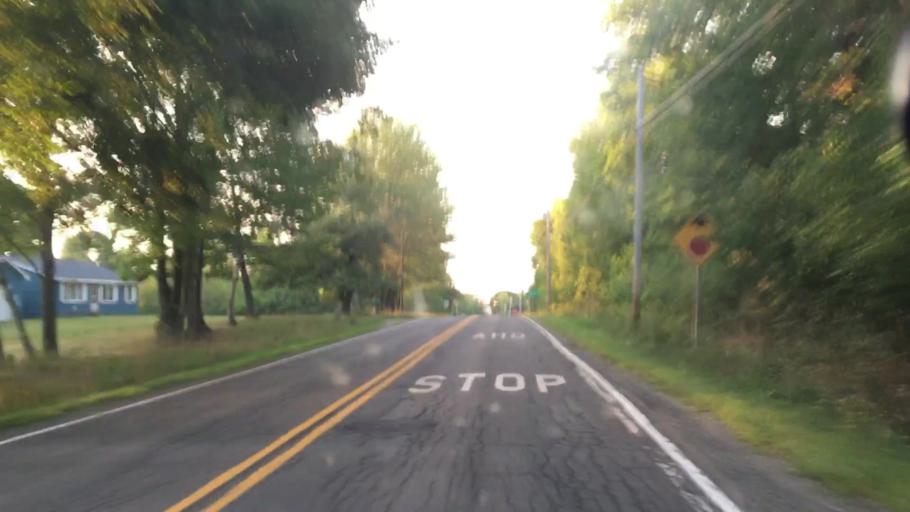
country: US
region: Maine
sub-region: Waldo County
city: Frankfort
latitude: 44.6966
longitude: -68.9434
